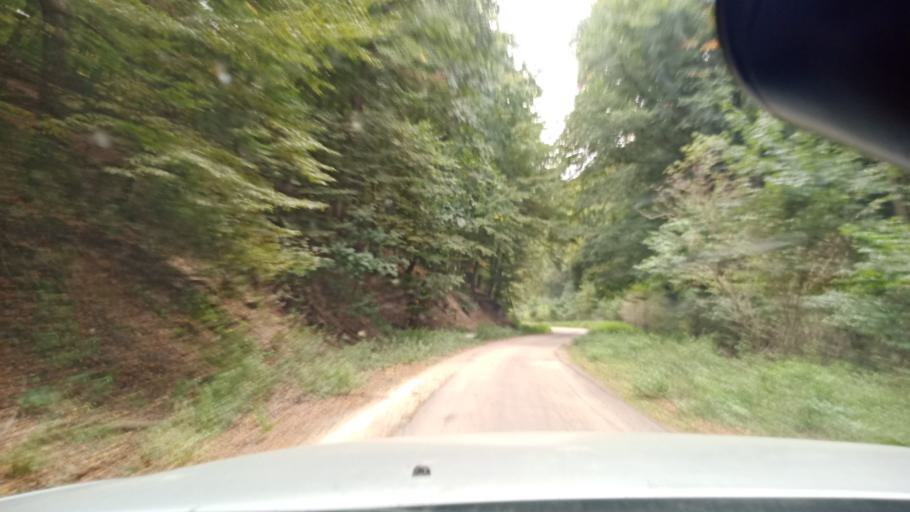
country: HU
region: Komarom-Esztergom
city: Oroszlany
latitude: 47.3953
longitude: 18.3131
